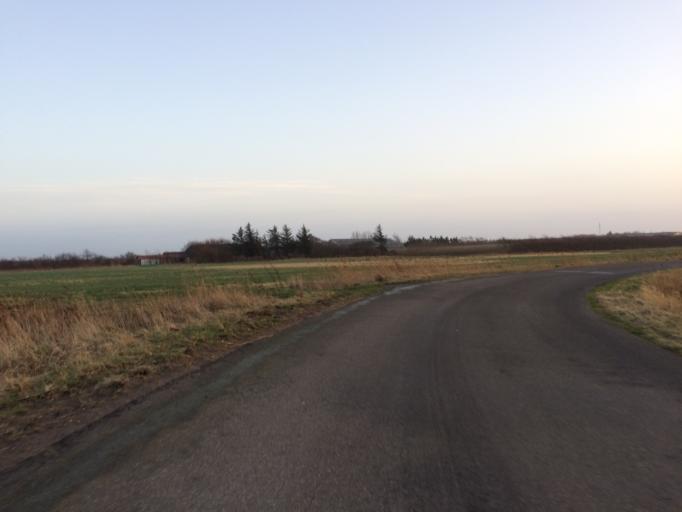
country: DK
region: Central Jutland
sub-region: Holstebro Kommune
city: Ulfborg
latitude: 56.2868
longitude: 8.2809
